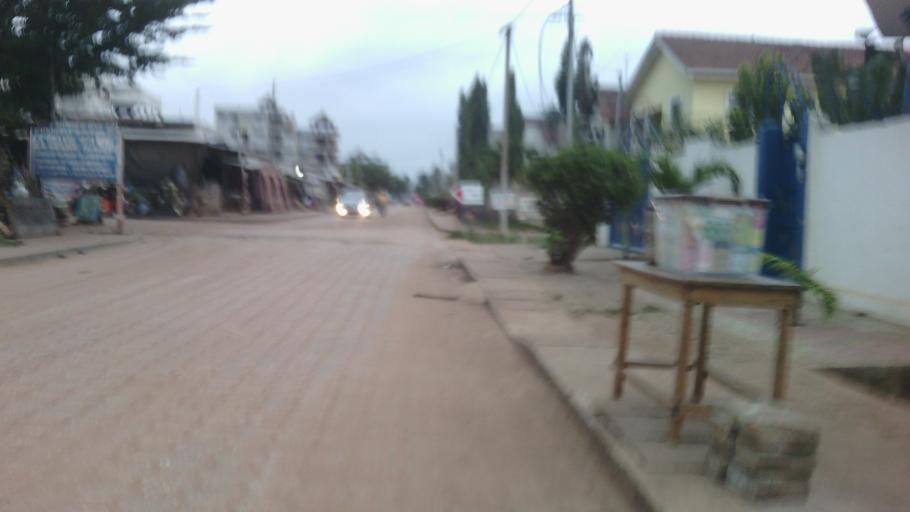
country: BJ
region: Atlantique
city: Abomey-Calavi
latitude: 6.4780
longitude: 2.3494
